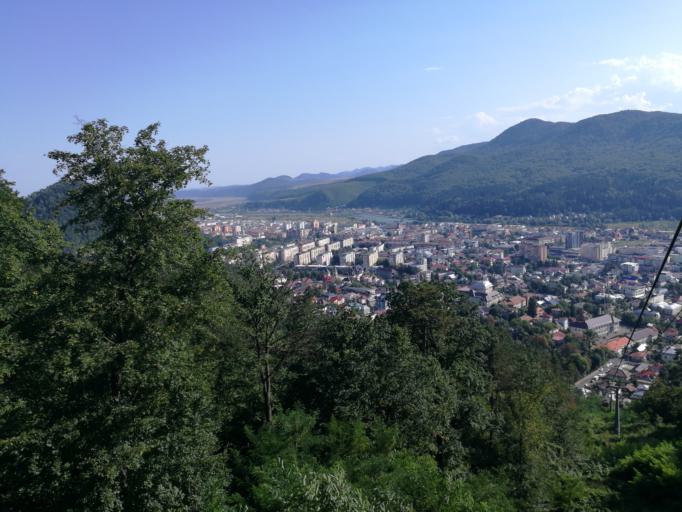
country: RO
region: Neamt
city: Piatra Neamt
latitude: 46.9404
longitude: 26.3657
